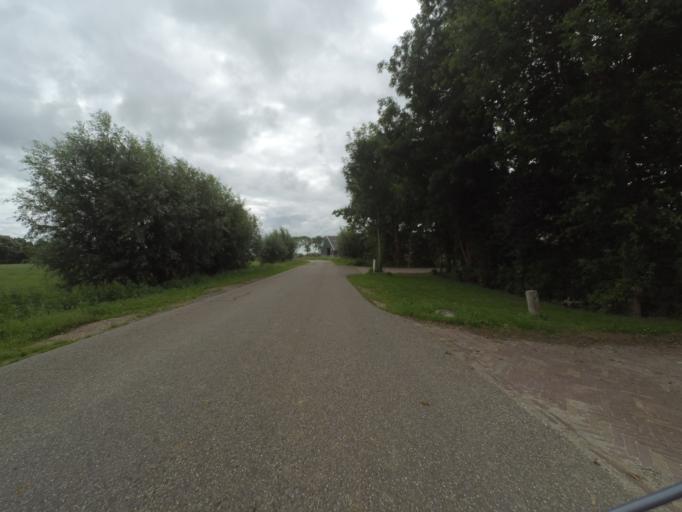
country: NL
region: Friesland
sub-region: Gemeente Kollumerland en Nieuwkruisland
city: Kollumerzwaag
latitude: 53.3196
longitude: 6.0928
